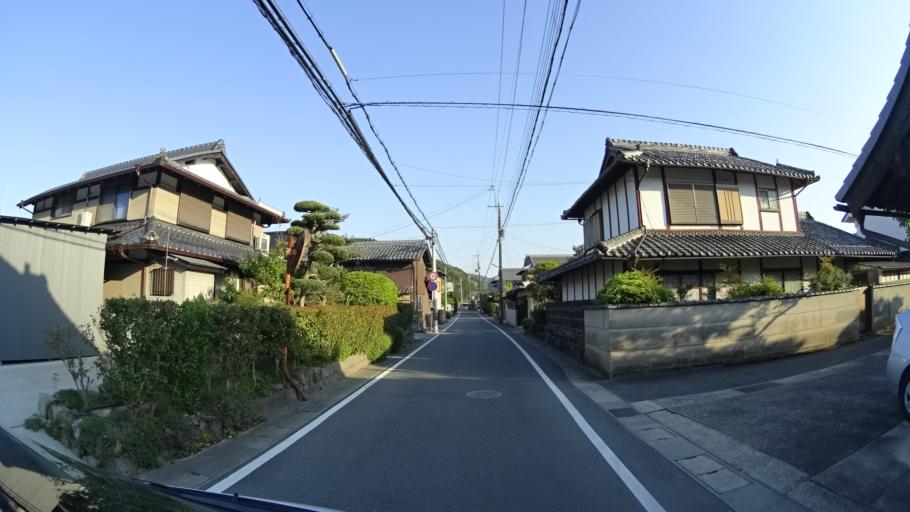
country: JP
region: Kyoto
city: Kameoka
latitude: 35.0895
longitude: 135.5106
